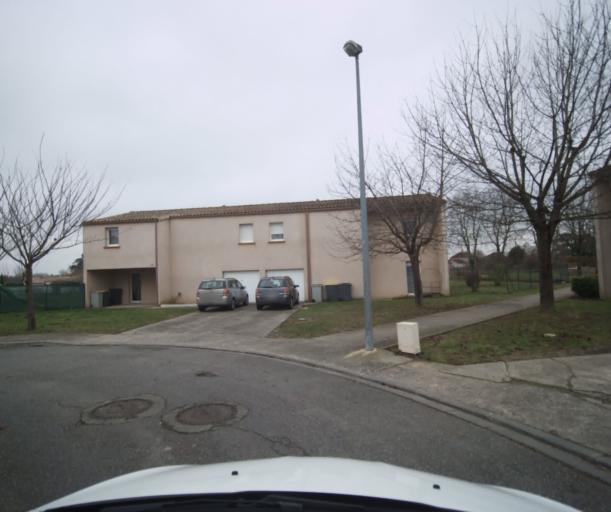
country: FR
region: Midi-Pyrenees
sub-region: Departement du Tarn-et-Garonne
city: Castelsarrasin
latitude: 44.0506
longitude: 1.1053
